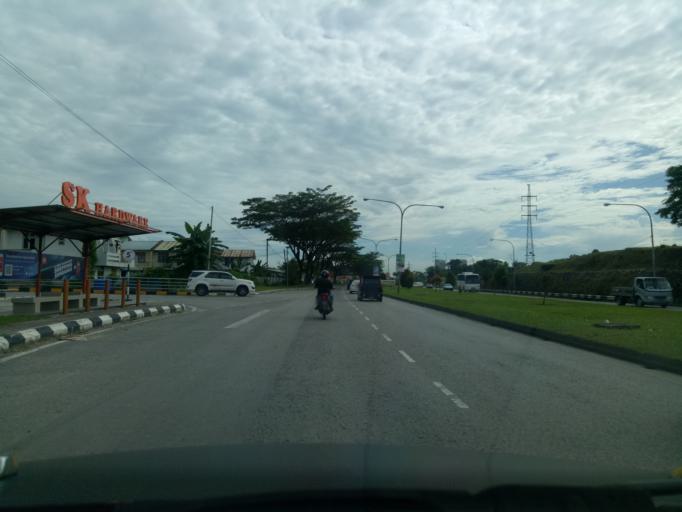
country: MY
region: Sarawak
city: Kuching
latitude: 1.4911
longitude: 110.3305
